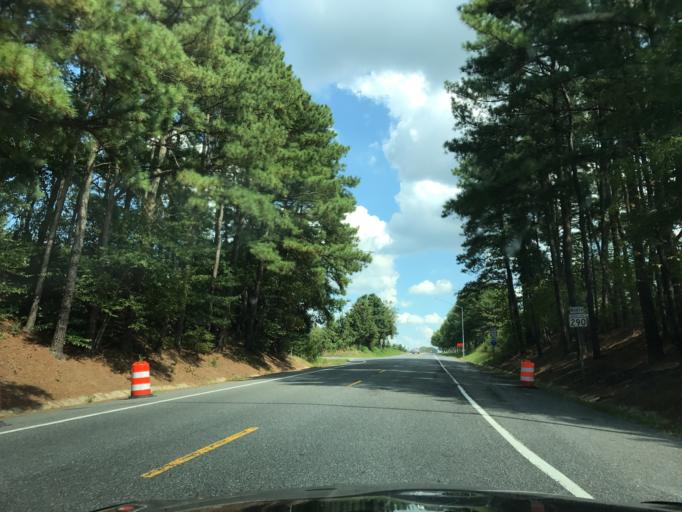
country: US
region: Delaware
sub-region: New Castle County
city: Townsend
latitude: 39.3651
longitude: -75.8149
